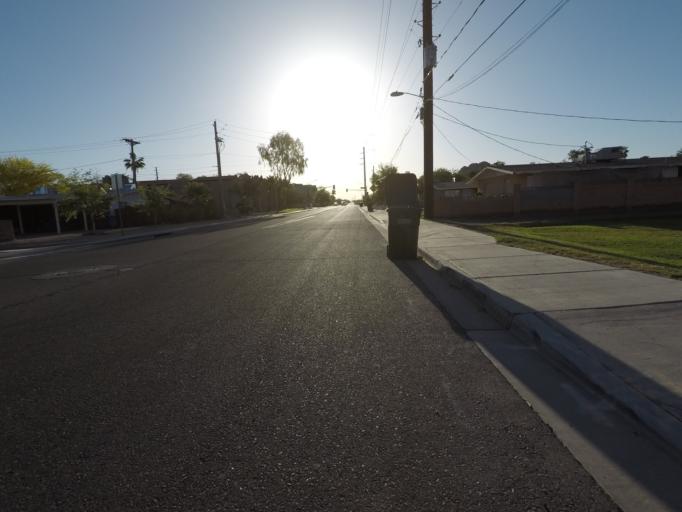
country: US
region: Arizona
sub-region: Maricopa County
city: Tempe Junction
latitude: 33.4728
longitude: -111.9710
